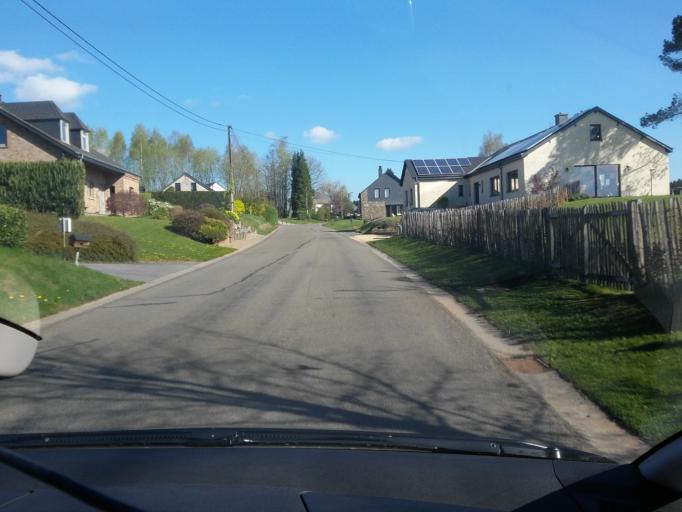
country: BE
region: Wallonia
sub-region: Province du Luxembourg
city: Libin
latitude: 49.9906
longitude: 5.2516
